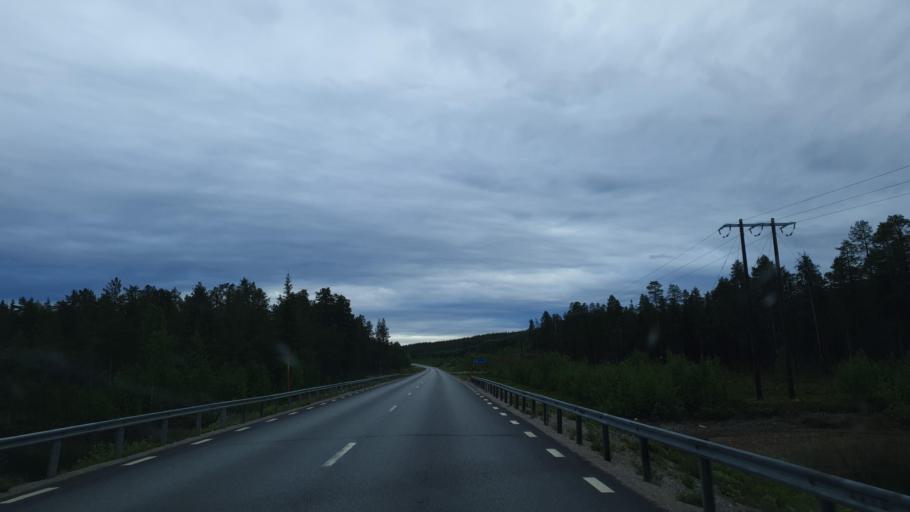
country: SE
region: Norrbotten
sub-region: Jokkmokks Kommun
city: Jokkmokk
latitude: 66.5044
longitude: 19.6742
